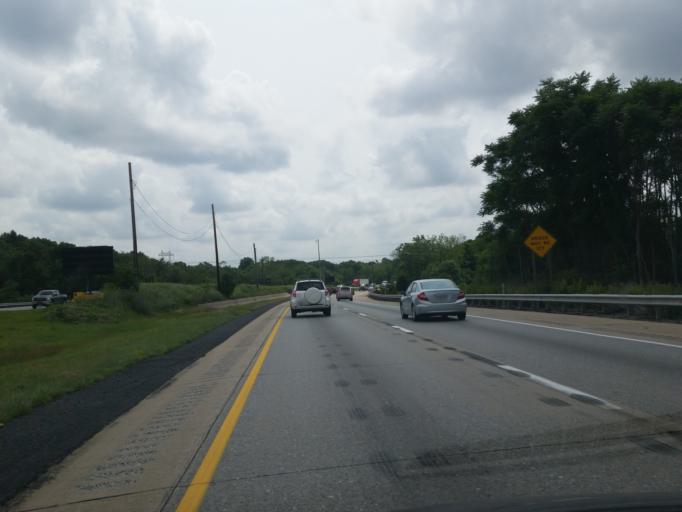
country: US
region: Pennsylvania
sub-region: Dauphin County
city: Skyline View
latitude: 40.3343
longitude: -76.7566
